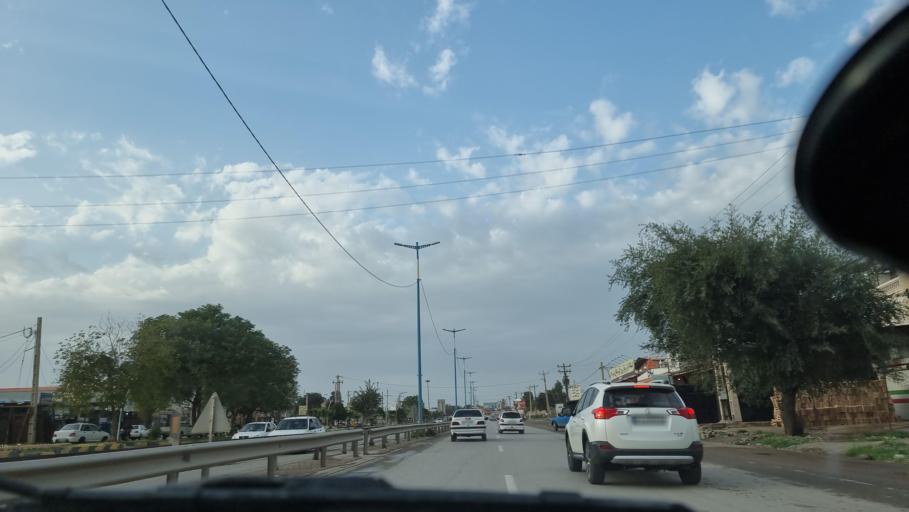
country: IR
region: Khuzestan
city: Boneh-ye Hoseyn Kaluli
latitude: 32.3023
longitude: 48.4284
